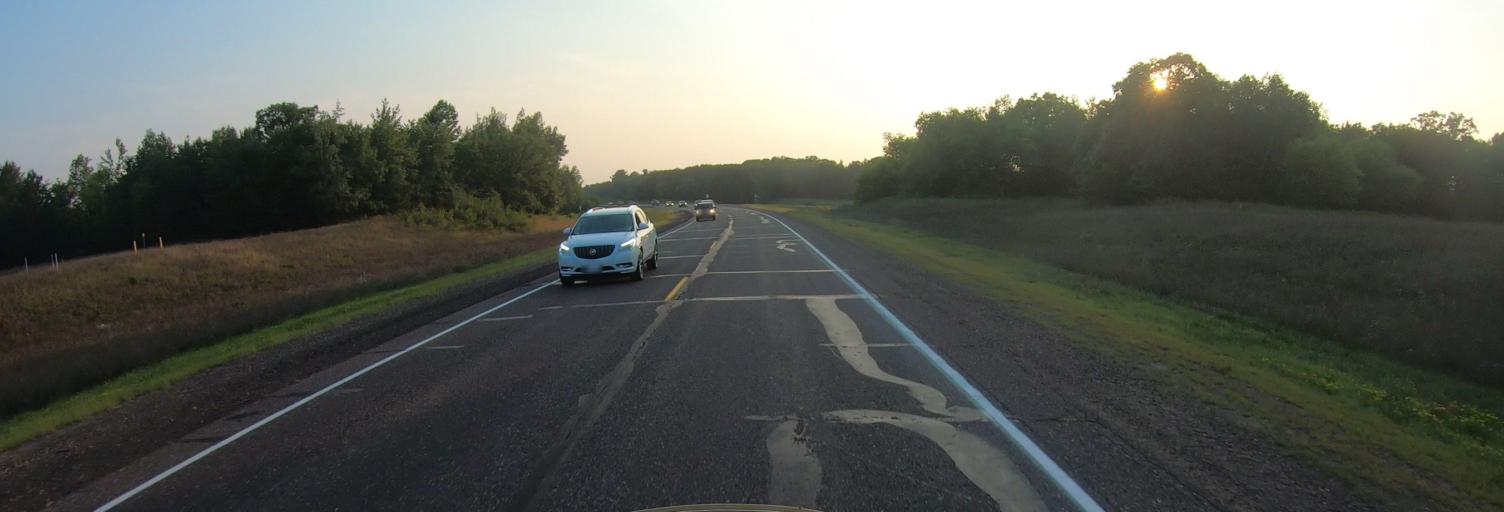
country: US
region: Wisconsin
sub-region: Burnett County
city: Siren
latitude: 45.7756
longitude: -92.4449
